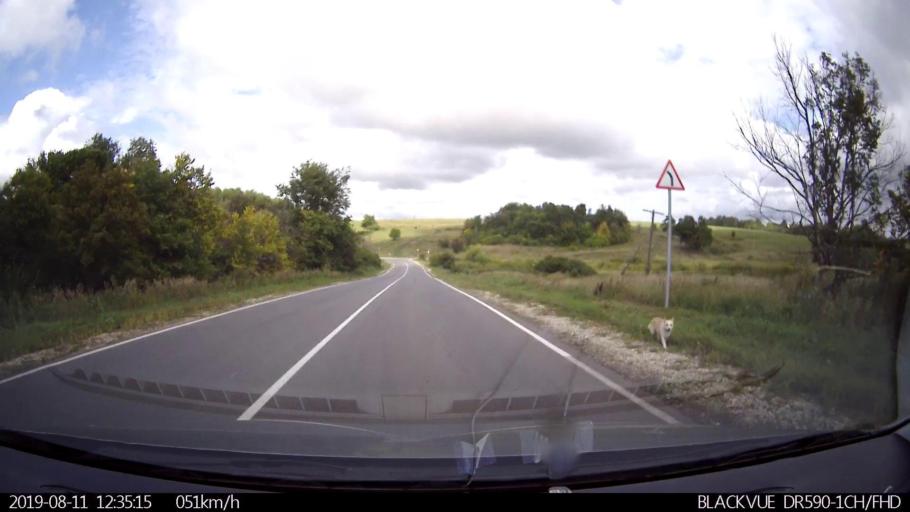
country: RU
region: Ulyanovsk
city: Ignatovka
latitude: 53.8232
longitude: 47.8343
